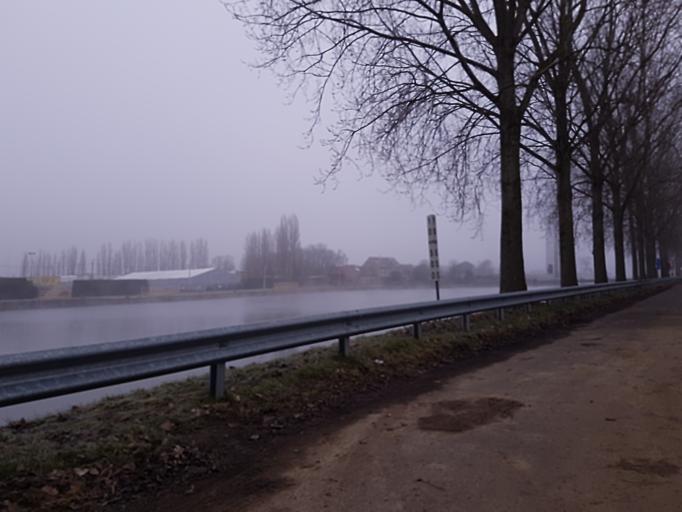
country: BE
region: Flanders
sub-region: Provincie Vlaams-Brabant
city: Vilvoorde
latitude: 50.9497
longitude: 4.4114
